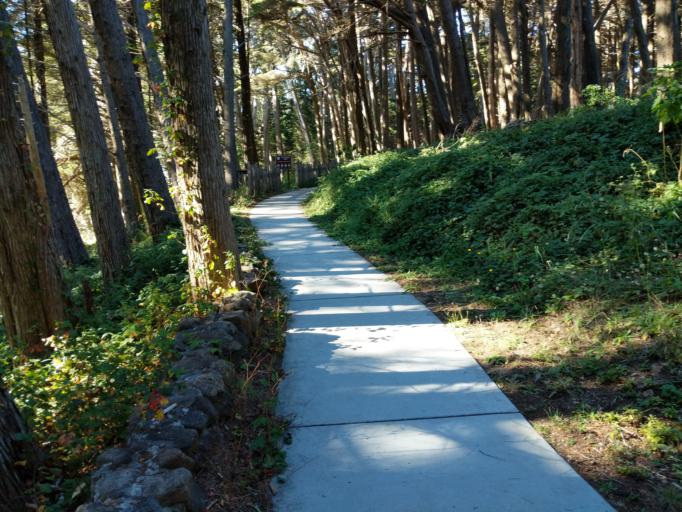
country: US
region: California
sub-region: Sonoma County
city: Monte Rio
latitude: 38.5158
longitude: -123.2456
